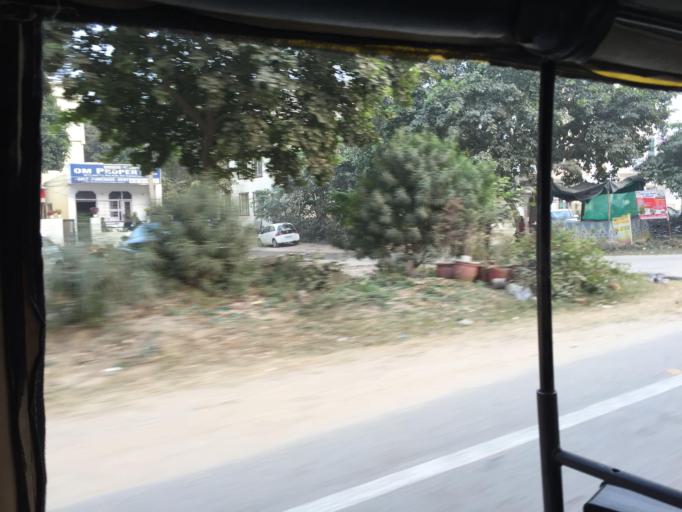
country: IN
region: Haryana
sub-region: Gurgaon
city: Gurgaon
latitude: 28.4265
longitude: 77.1053
